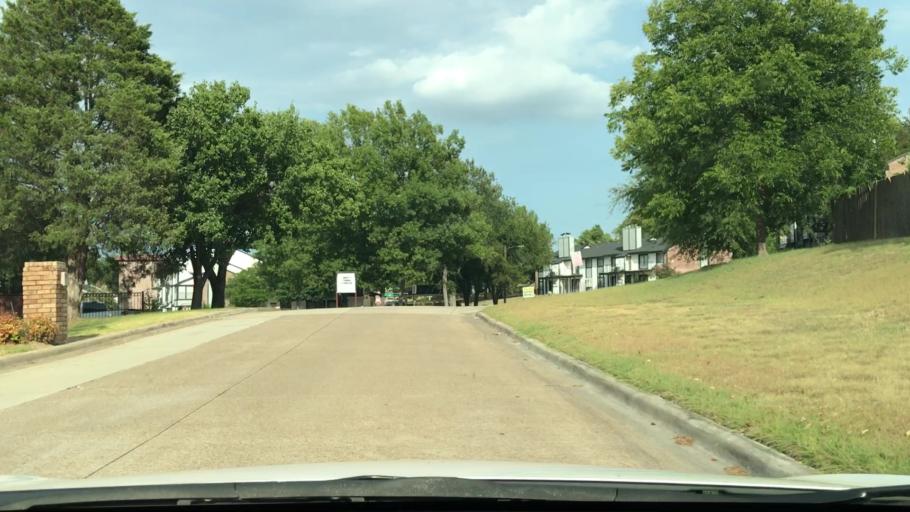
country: US
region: Texas
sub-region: Rockwall County
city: Rockwall
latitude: 32.9274
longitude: -96.4635
